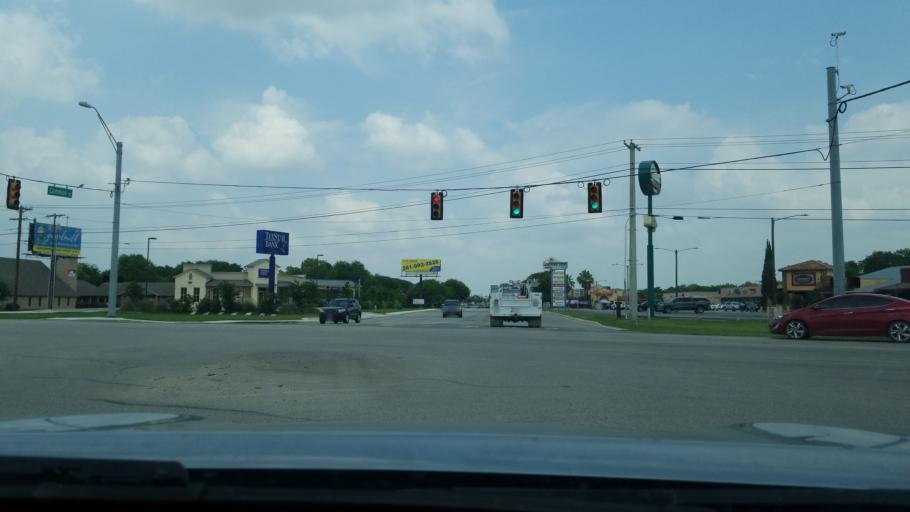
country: US
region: Texas
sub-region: Comal County
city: New Braunfels
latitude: 29.7199
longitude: -98.1041
